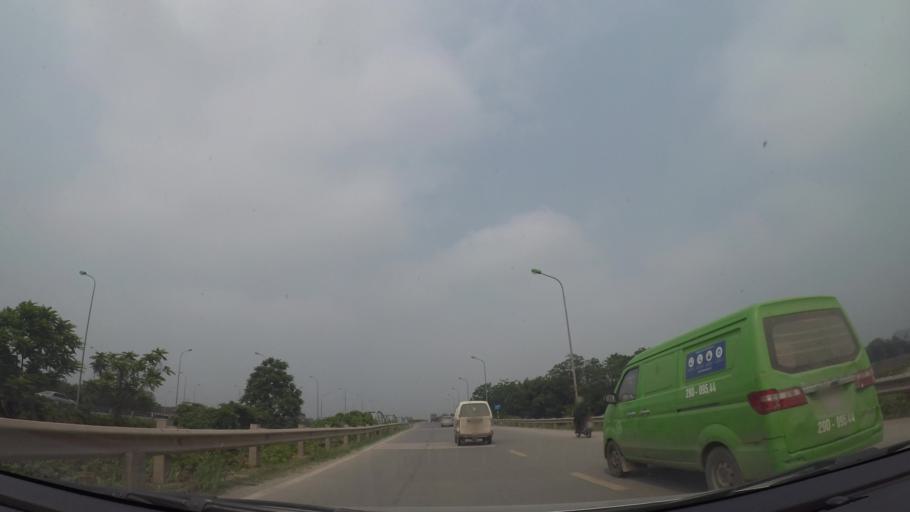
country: VN
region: Ha Noi
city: Quoc Oai
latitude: 21.0038
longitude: 105.6661
